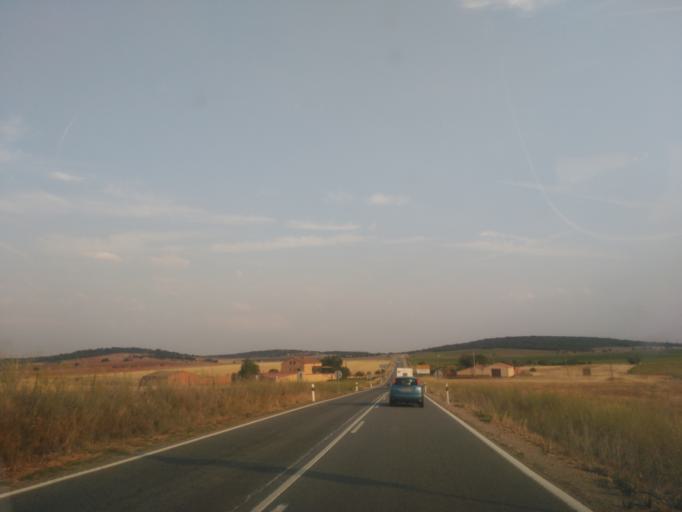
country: ES
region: Castille and Leon
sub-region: Provincia de Zamora
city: Montamarta
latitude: 41.6965
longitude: -5.8145
